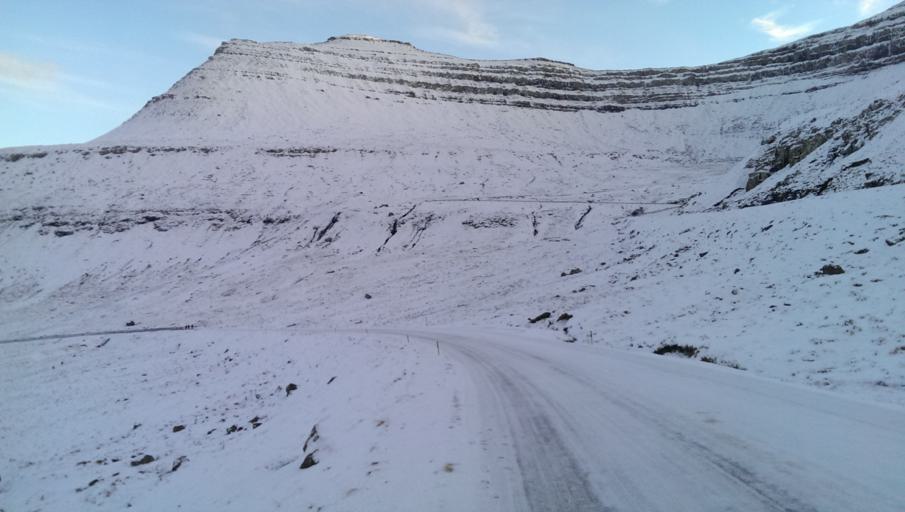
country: FO
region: Eysturoy
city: Fuglafjordur
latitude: 62.2547
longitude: -6.8662
